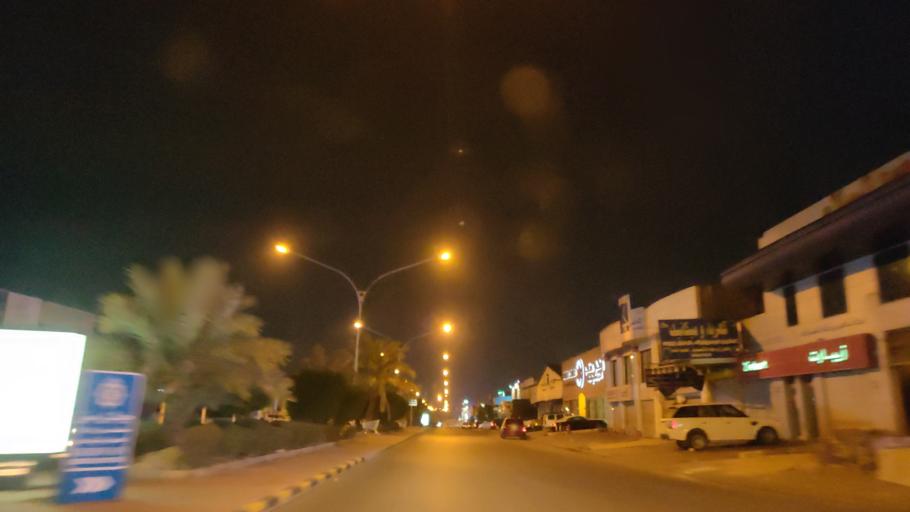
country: KW
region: Al Asimah
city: Ar Rabiyah
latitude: 29.3075
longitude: 47.9357
